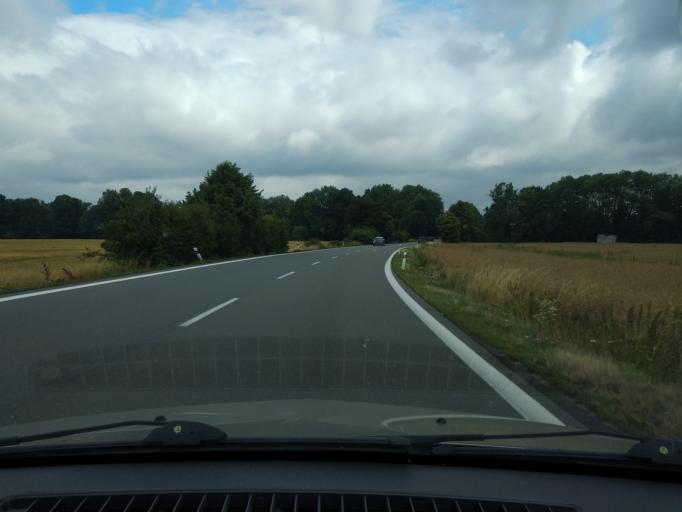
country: CZ
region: Olomoucky
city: Postrelmov
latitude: 49.9251
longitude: 16.9185
